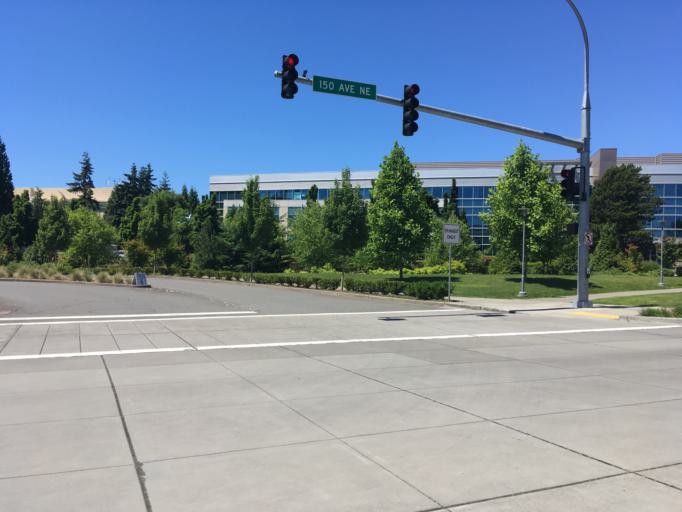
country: US
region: Washington
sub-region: King County
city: Redmond
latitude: 47.6432
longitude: -122.1394
